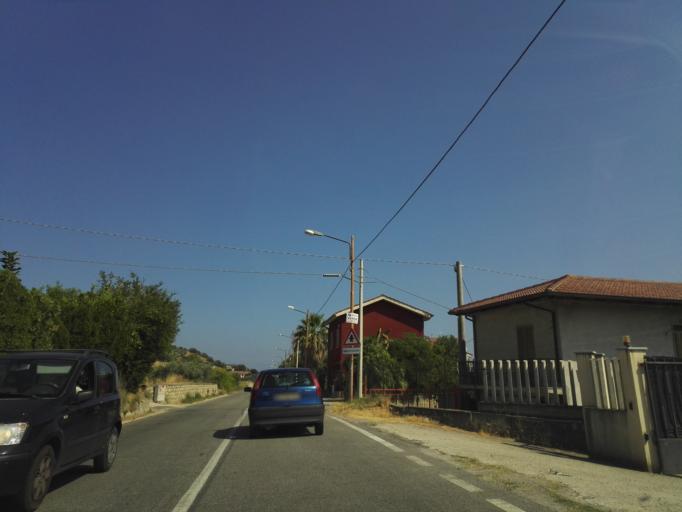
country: IT
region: Calabria
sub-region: Provincia di Reggio Calabria
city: Monasterace
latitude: 38.4444
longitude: 16.5381
